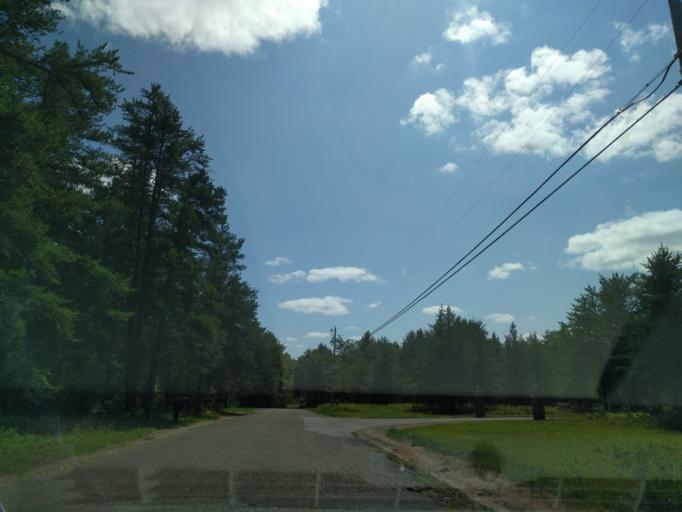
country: US
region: Michigan
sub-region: Marquette County
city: K. I. Sawyer Air Force Base
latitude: 46.2809
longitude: -87.3663
